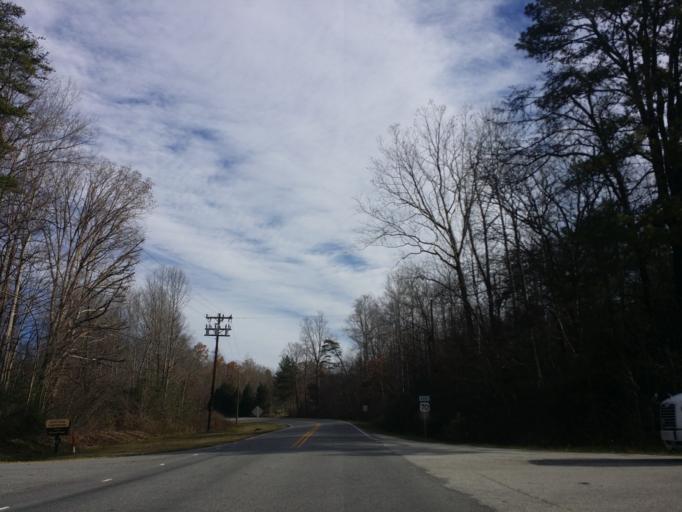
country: US
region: North Carolina
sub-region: McDowell County
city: West Marion
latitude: 35.6460
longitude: -82.1578
